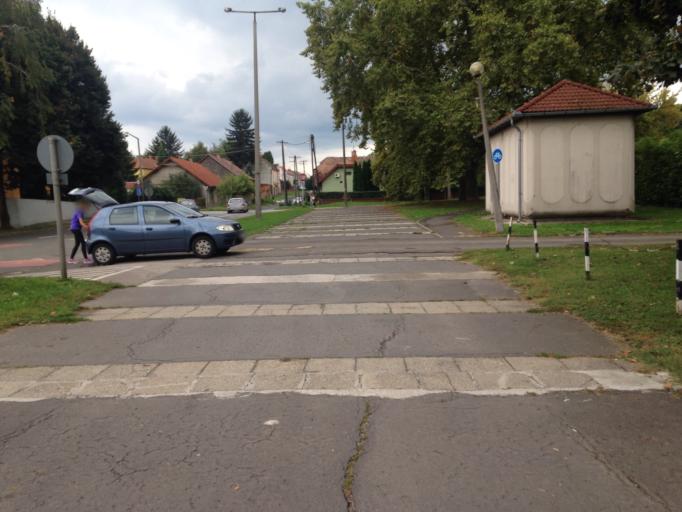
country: HU
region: Somogy
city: Kaposvar
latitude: 46.3686
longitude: 17.7946
